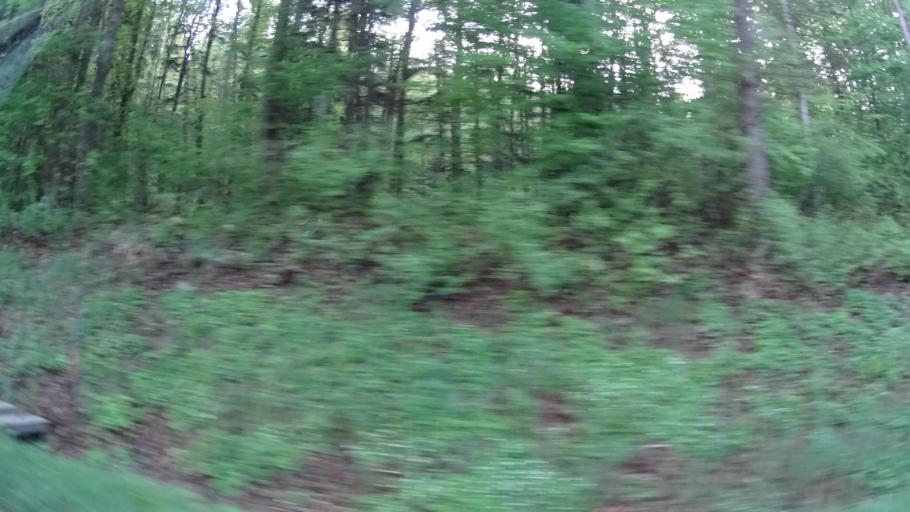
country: DE
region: Baden-Wuerttemberg
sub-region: Karlsruhe Region
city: Empfingen
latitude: 48.4268
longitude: 8.7654
